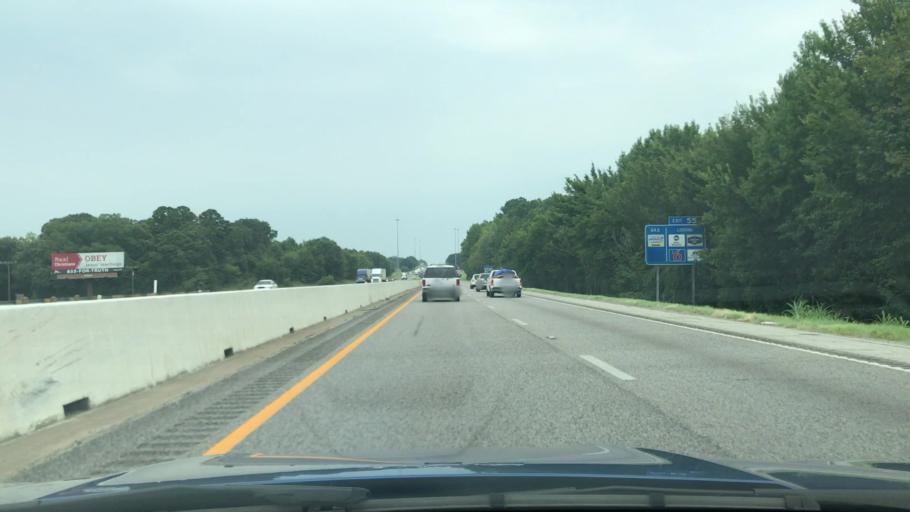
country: US
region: Texas
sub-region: Smith County
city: Lindale
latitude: 32.4685
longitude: -95.3999
